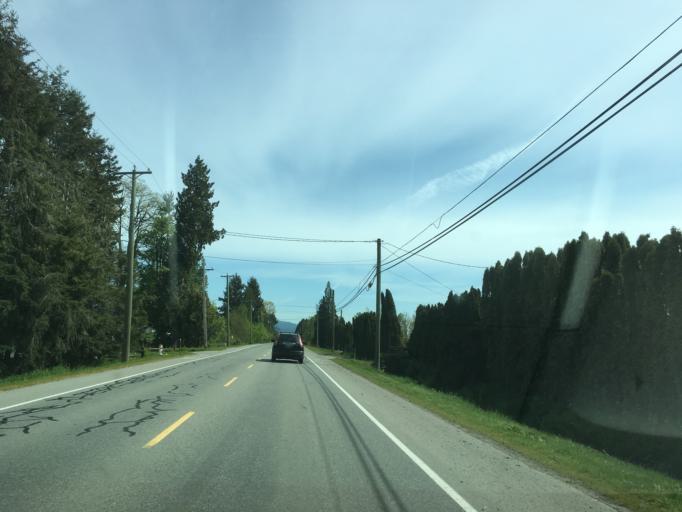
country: CA
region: British Columbia
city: Pitt Meadows
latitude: 49.2442
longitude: -122.6977
